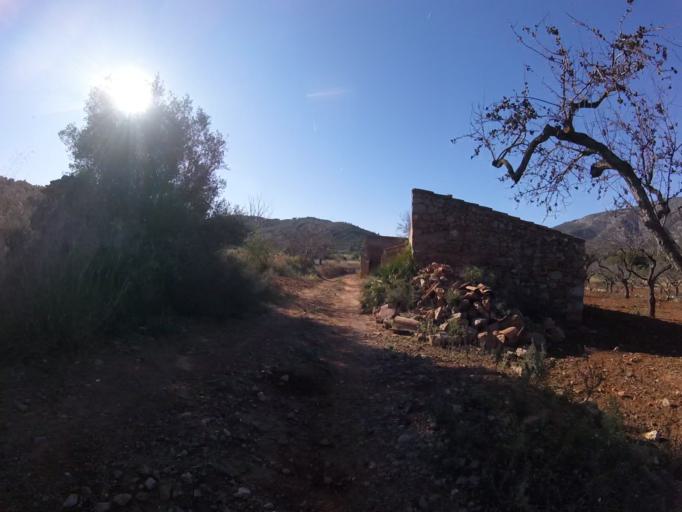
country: ES
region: Valencia
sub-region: Provincia de Castello
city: Orpesa/Oropesa del Mar
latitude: 40.1215
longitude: 0.1173
